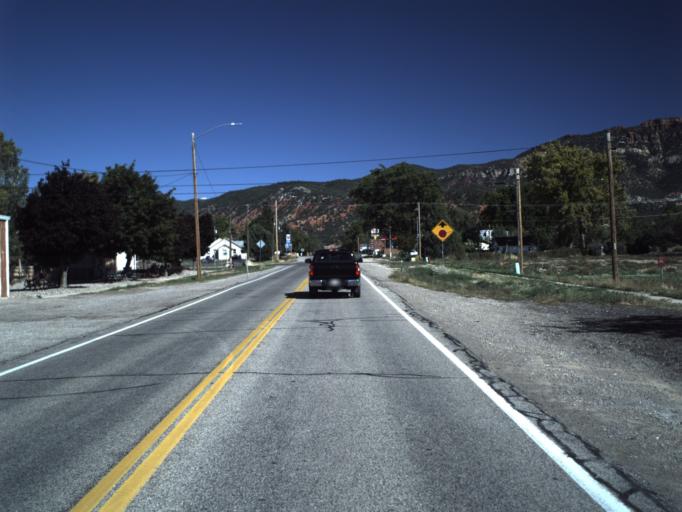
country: US
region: Utah
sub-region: Iron County
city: Parowan
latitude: 37.8388
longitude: -112.8315
